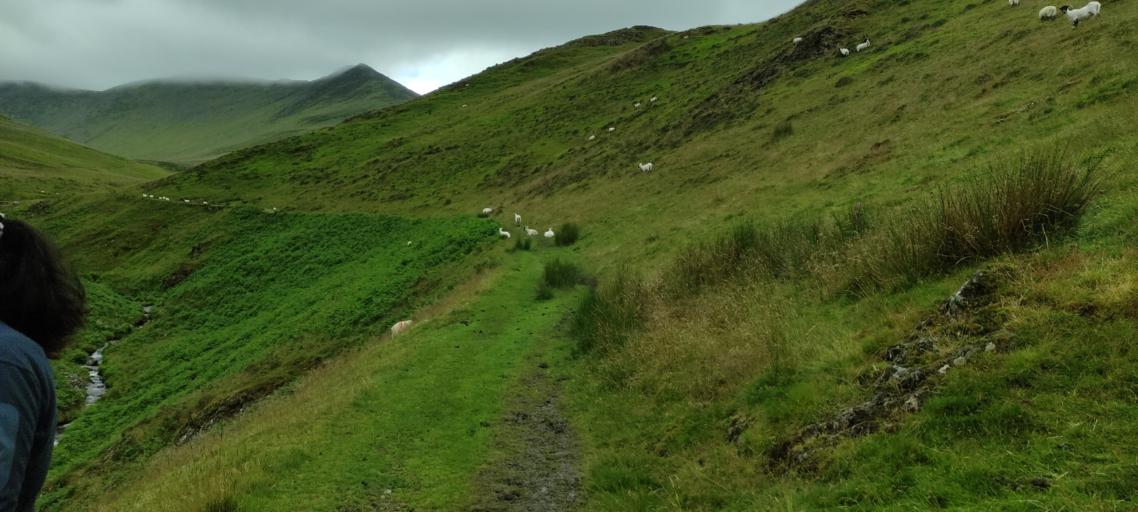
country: GB
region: England
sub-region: Cumbria
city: Keswick
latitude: 54.6654
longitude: -3.1777
